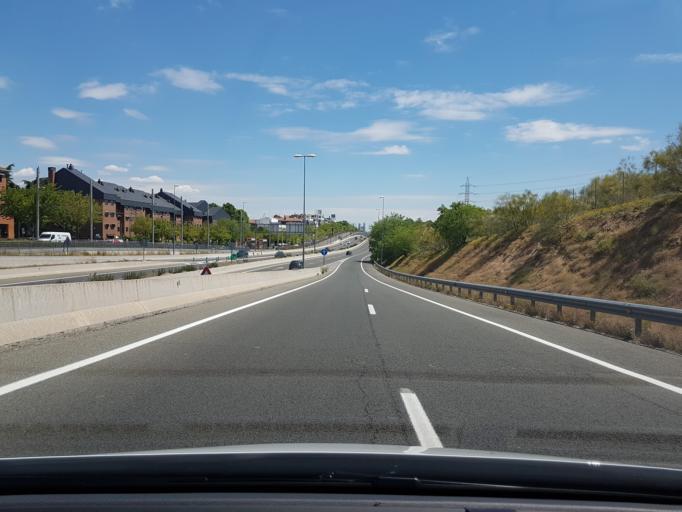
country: ES
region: Madrid
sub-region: Provincia de Madrid
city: Pozuelo de Alarcon
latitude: 40.4297
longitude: -3.8091
